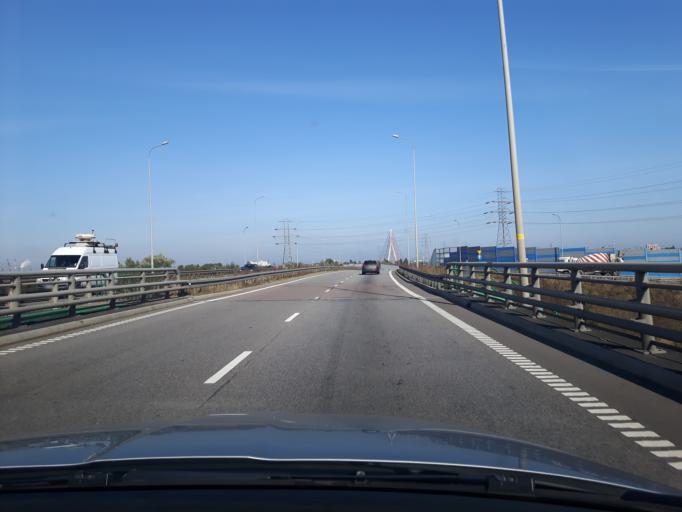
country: PL
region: Pomeranian Voivodeship
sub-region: Gdansk
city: Gdansk
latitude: 54.3430
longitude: 18.6979
